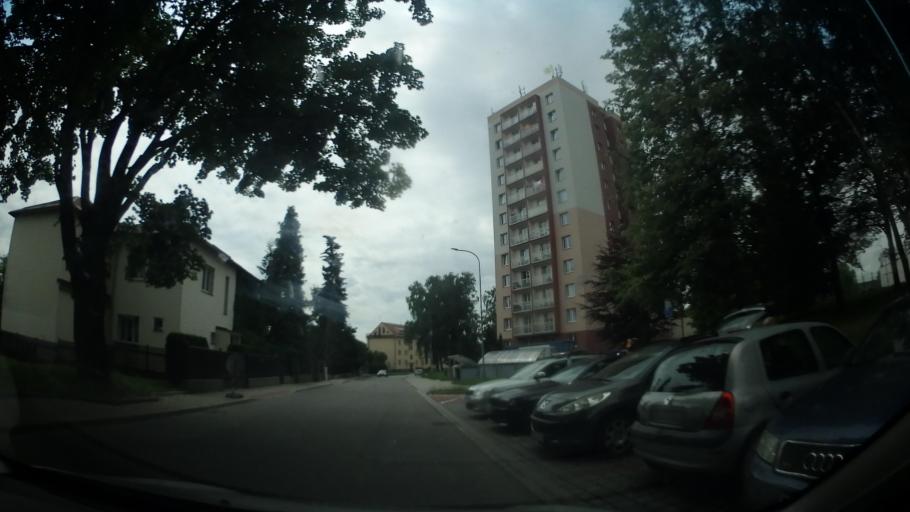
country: CZ
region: Vysocina
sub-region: Okres Zd'ar nad Sazavou
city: Nove Mesto na Morave
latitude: 49.5652
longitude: 16.0749
